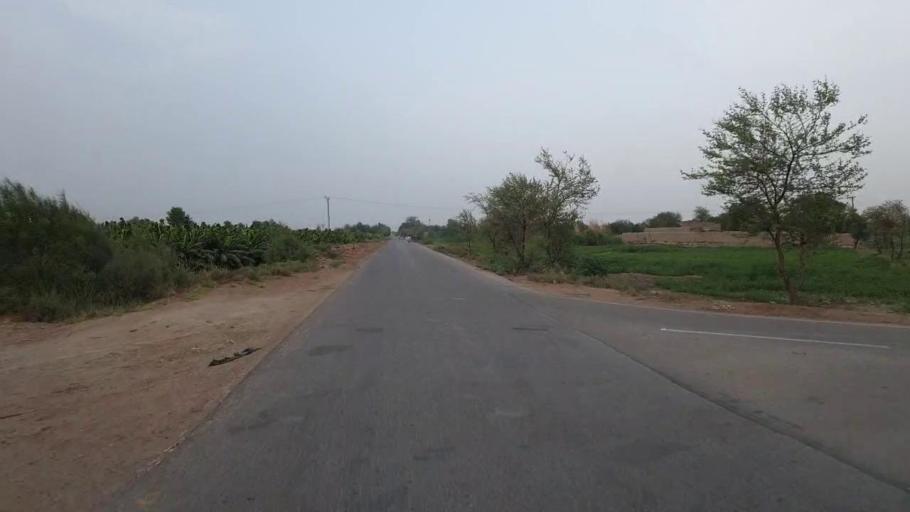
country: PK
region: Sindh
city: Daur
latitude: 26.4079
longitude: 68.2312
